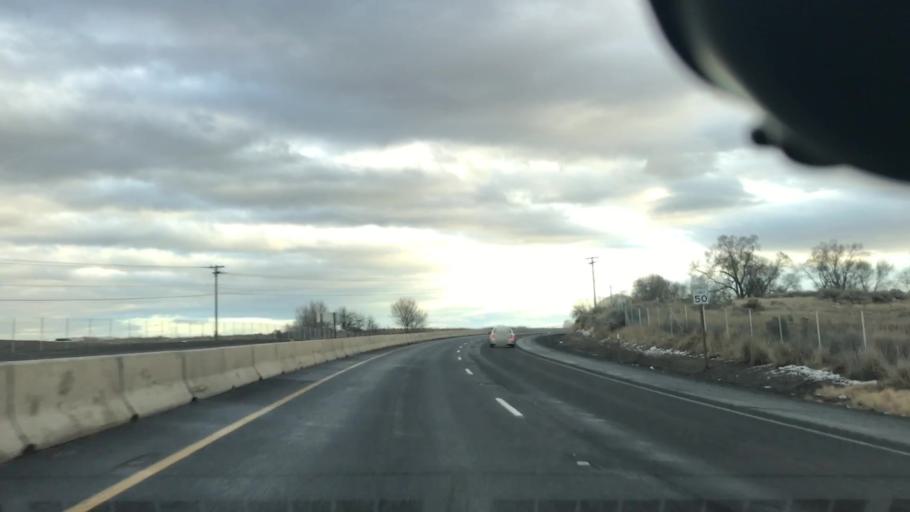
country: US
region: Washington
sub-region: Grant County
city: Moses Lake
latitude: 47.1375
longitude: -119.2583
